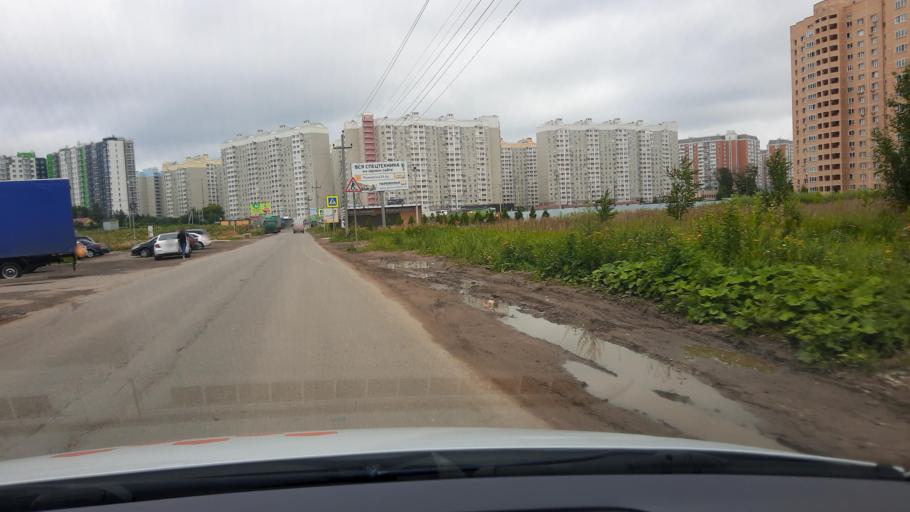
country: RU
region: Moskovskaya
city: Vidnoye
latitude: 55.5345
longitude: 37.7167
